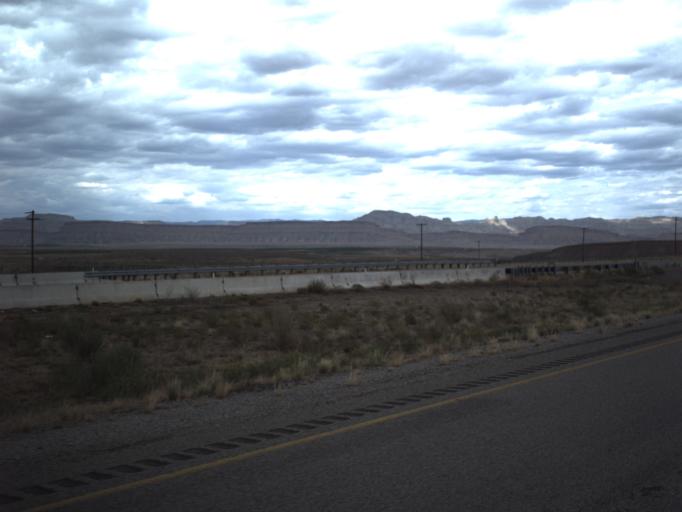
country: US
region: Utah
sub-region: Carbon County
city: East Carbon City
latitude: 38.9744
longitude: -110.1368
